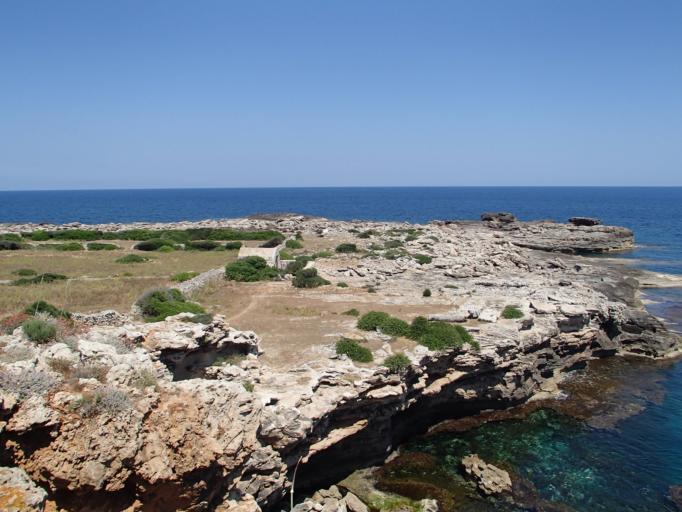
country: ES
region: Balearic Islands
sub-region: Illes Balears
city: Es Castell
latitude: 39.8489
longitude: 4.3055
